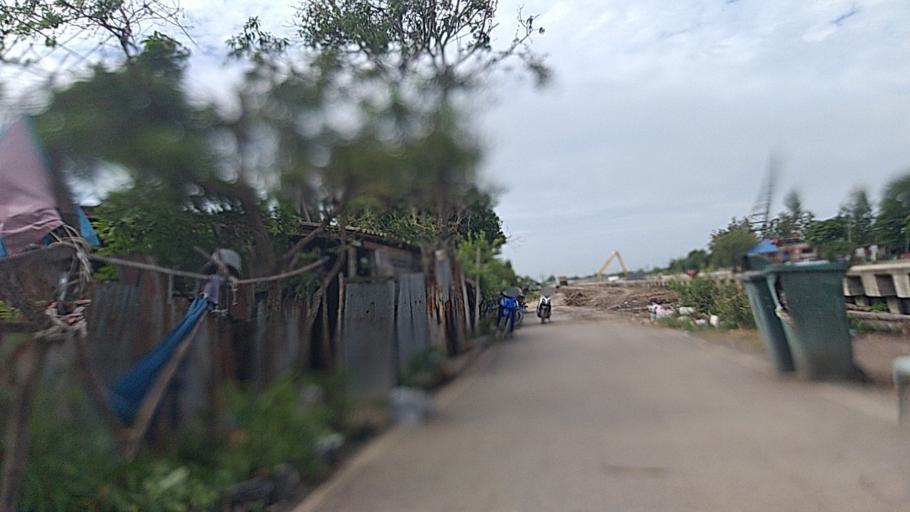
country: TH
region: Pathum Thani
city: Nong Suea
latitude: 14.0733
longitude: 100.8925
